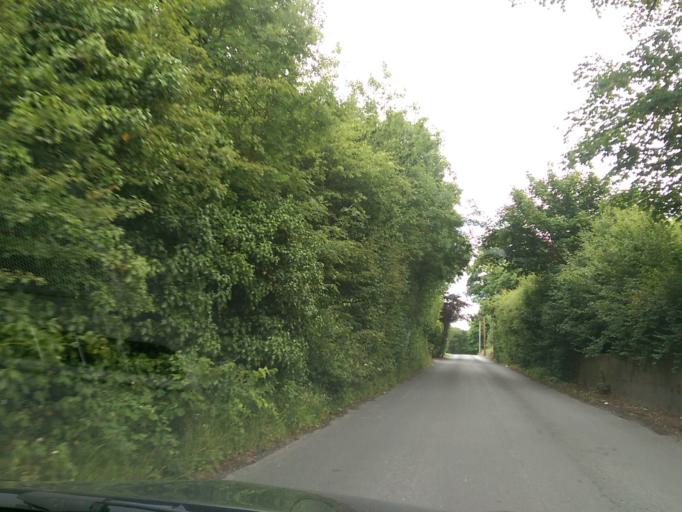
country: IE
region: Munster
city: Thurles
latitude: 52.6639
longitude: -7.7969
